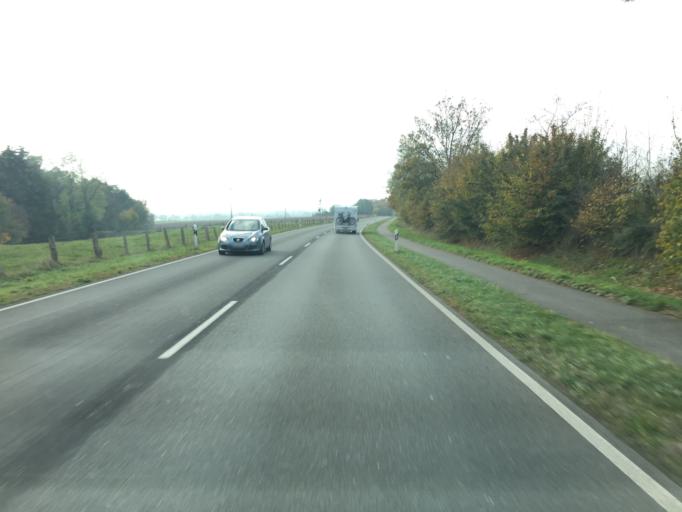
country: DE
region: North Rhine-Westphalia
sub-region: Regierungsbezirk Dusseldorf
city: Sonsbeck
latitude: 51.6246
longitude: 6.3899
